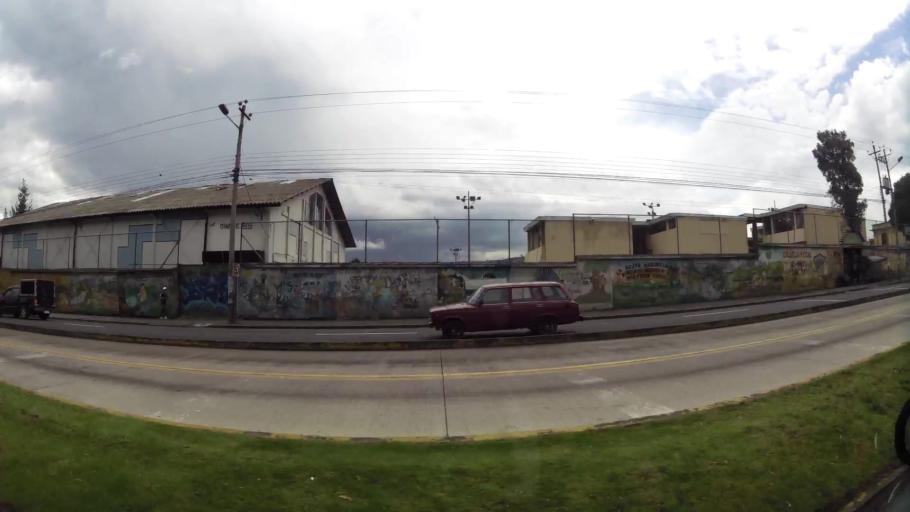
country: EC
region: Pichincha
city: Quito
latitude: -0.2741
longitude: -78.5525
